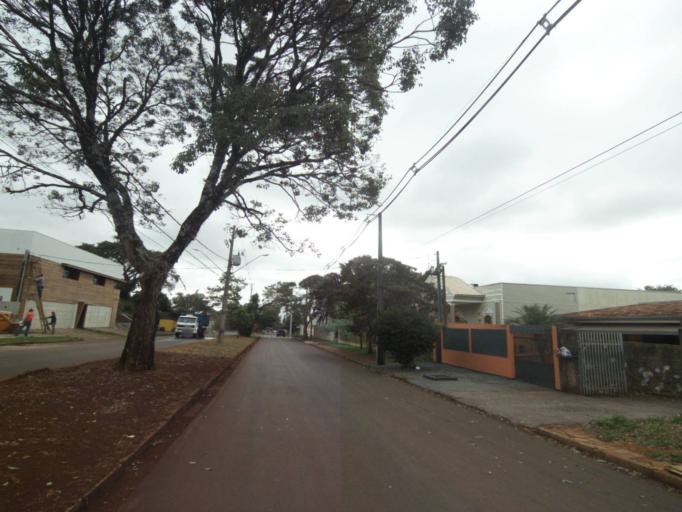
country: BR
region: Parana
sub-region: Campo Mourao
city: Campo Mourao
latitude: -24.0416
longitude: -52.3672
